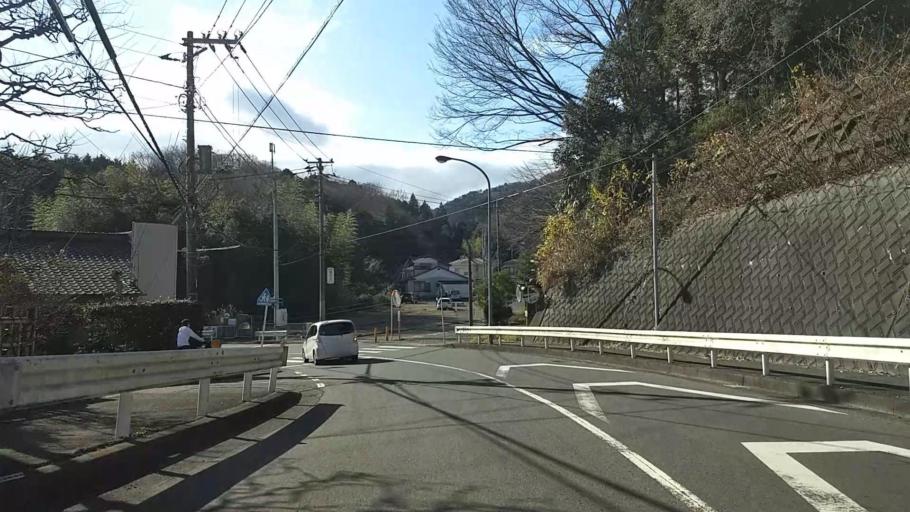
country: JP
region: Kanagawa
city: Atsugi
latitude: 35.4703
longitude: 139.2874
